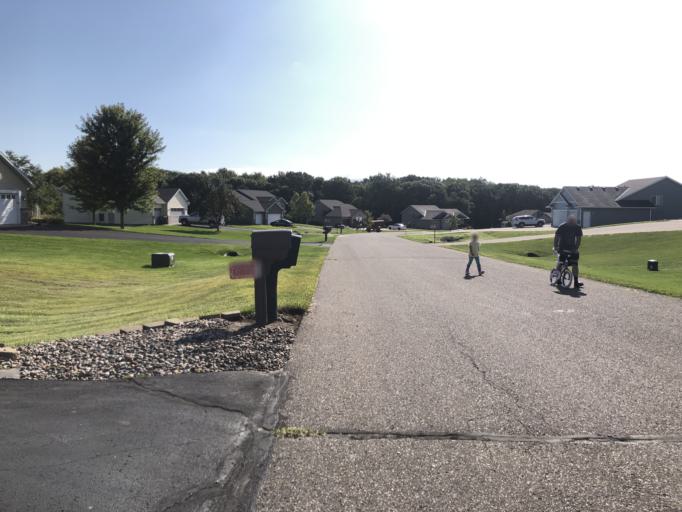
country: US
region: Minnesota
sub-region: Sherburne County
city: Becker
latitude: 45.4253
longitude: -93.8352
